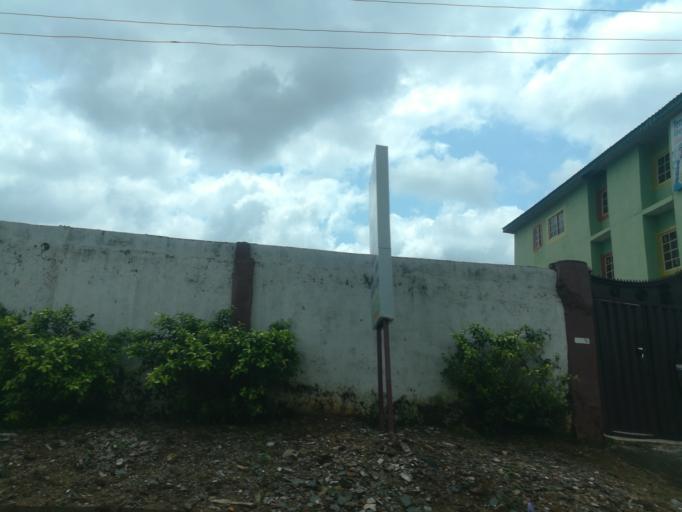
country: NG
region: Oyo
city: Ibadan
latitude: 7.3666
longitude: 3.8310
